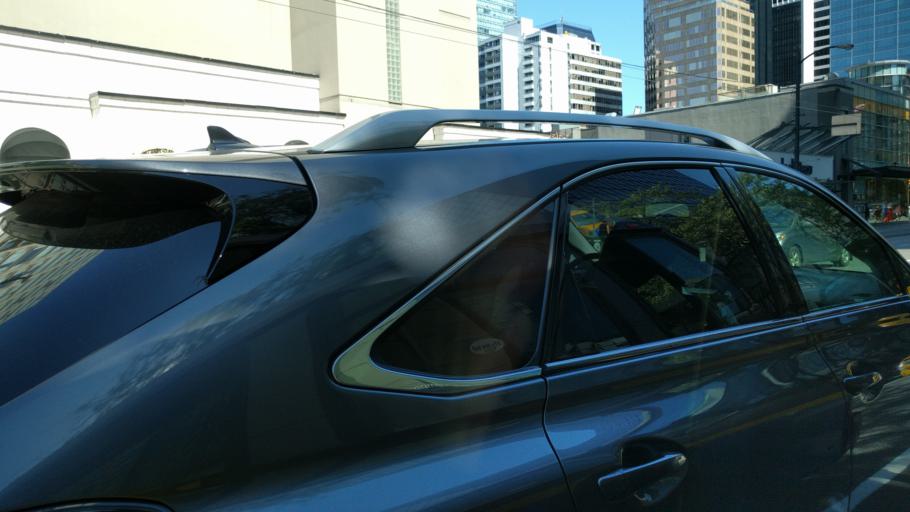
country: CA
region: British Columbia
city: West End
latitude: 49.2829
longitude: -123.1240
